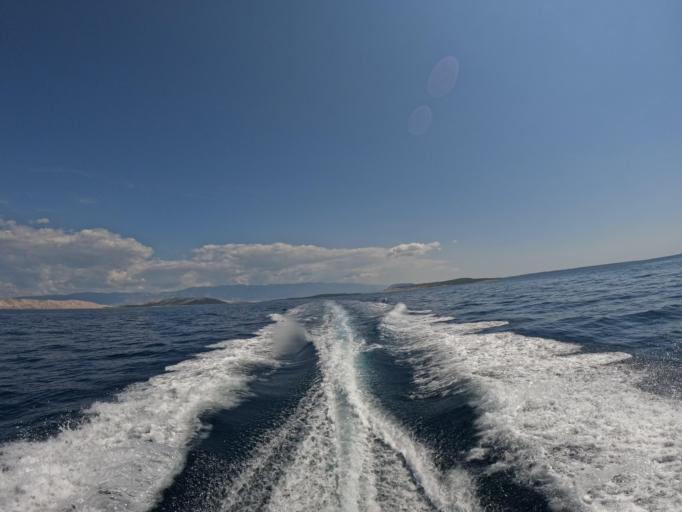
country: HR
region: Primorsko-Goranska
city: Lopar
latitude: 44.8771
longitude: 14.6586
